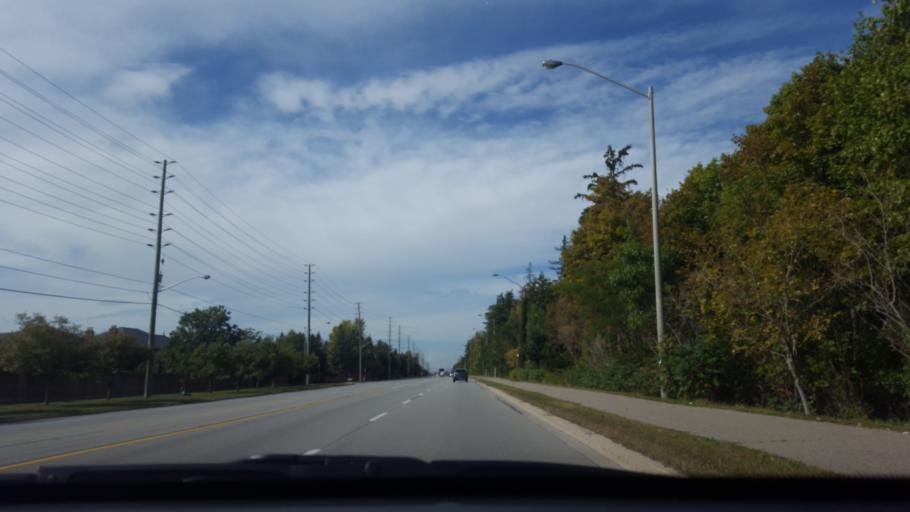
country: CA
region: Ontario
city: Vaughan
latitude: 43.8107
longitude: -79.5903
